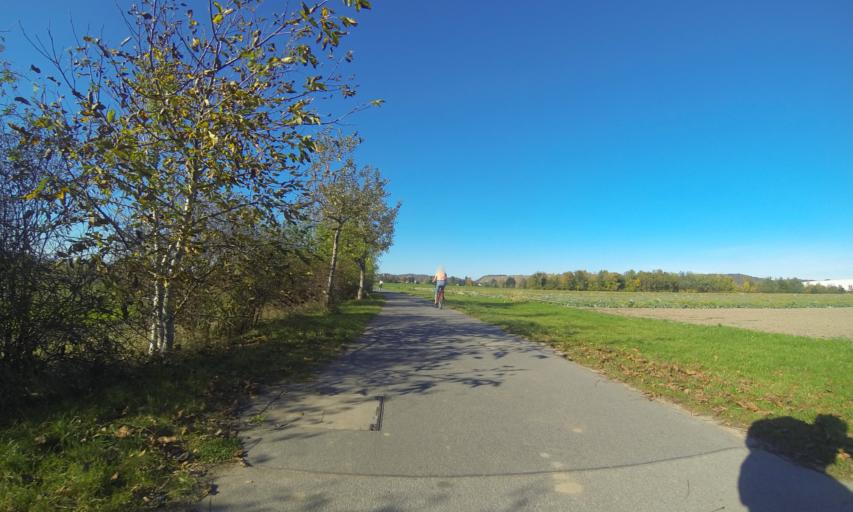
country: DE
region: Saxony
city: Radebeul
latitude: 51.0871
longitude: 13.6686
